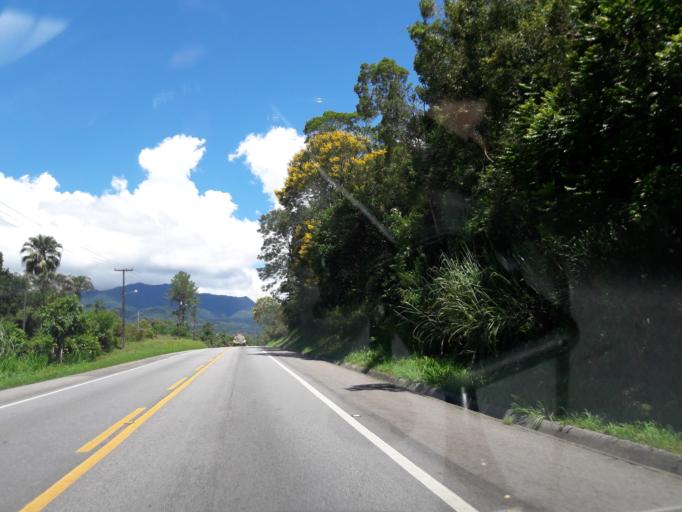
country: BR
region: Parana
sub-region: Antonina
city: Antonina
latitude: -25.5342
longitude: -48.7940
